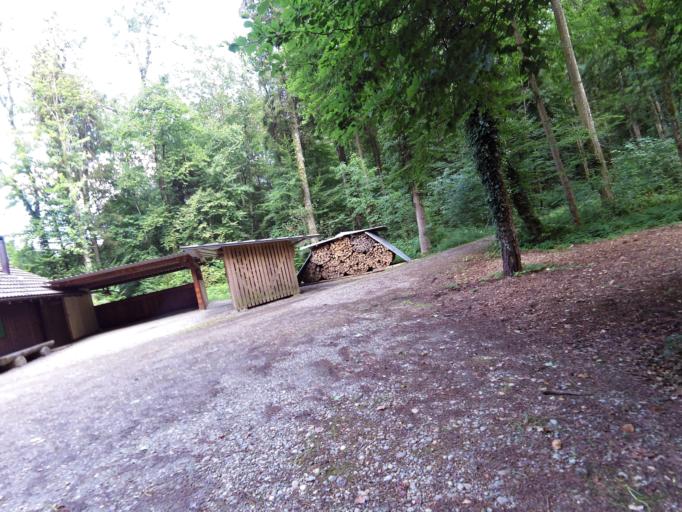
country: CH
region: Thurgau
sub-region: Kreuzlingen District
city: Ermatingen
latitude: 47.6471
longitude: 9.0986
